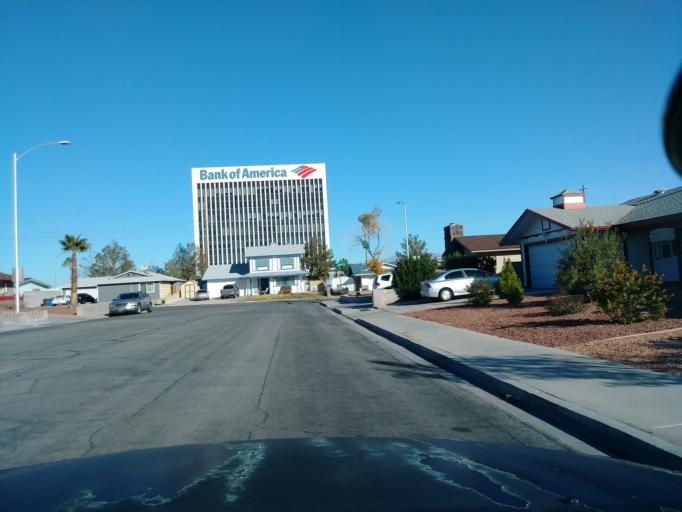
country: US
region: Nevada
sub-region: Clark County
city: Spring Valley
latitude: 36.1728
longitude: -115.2469
